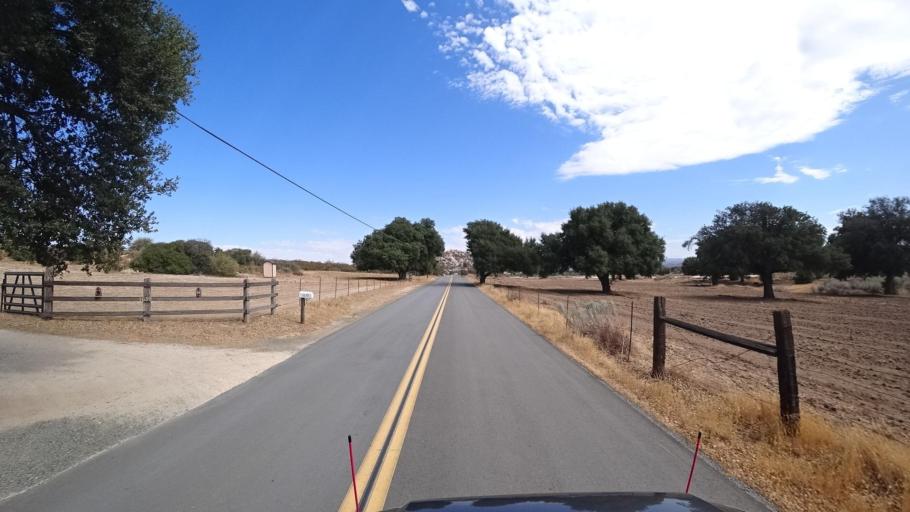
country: MX
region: Baja California
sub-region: Tecate
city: Cereso del Hongo
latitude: 32.6420
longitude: -116.2760
